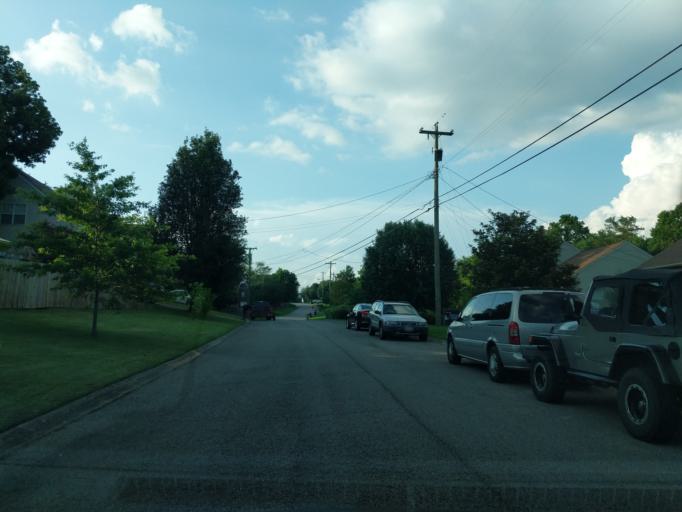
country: US
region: Tennessee
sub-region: Sumner County
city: Hendersonville
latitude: 36.2941
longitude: -86.6387
